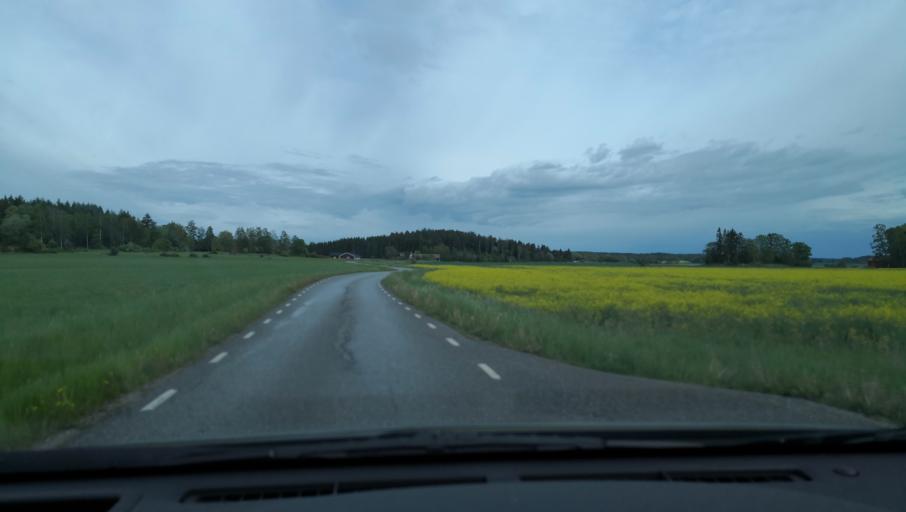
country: SE
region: Uppsala
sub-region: Enkopings Kommun
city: Orsundsbro
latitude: 59.7072
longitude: 17.3804
